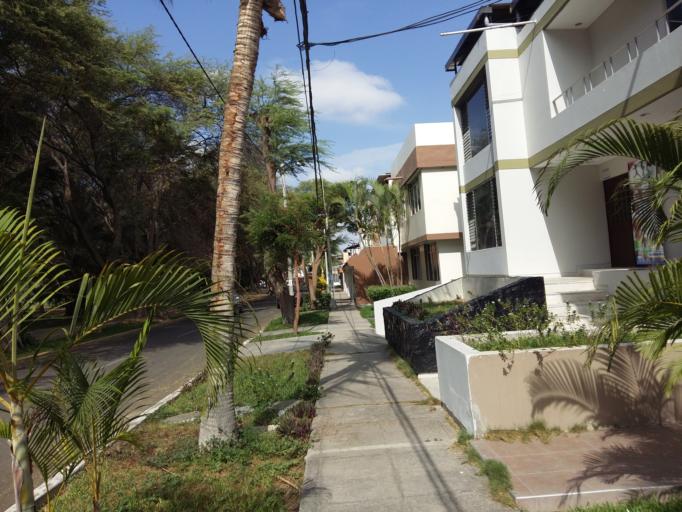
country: PE
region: Piura
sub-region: Provincia de Piura
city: Piura
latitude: -5.1904
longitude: -80.6209
